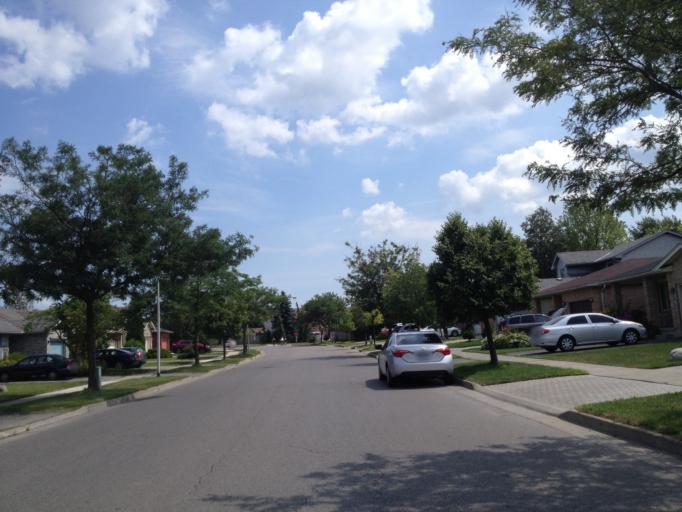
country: CA
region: Ontario
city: London
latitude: 42.9955
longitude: -81.3141
